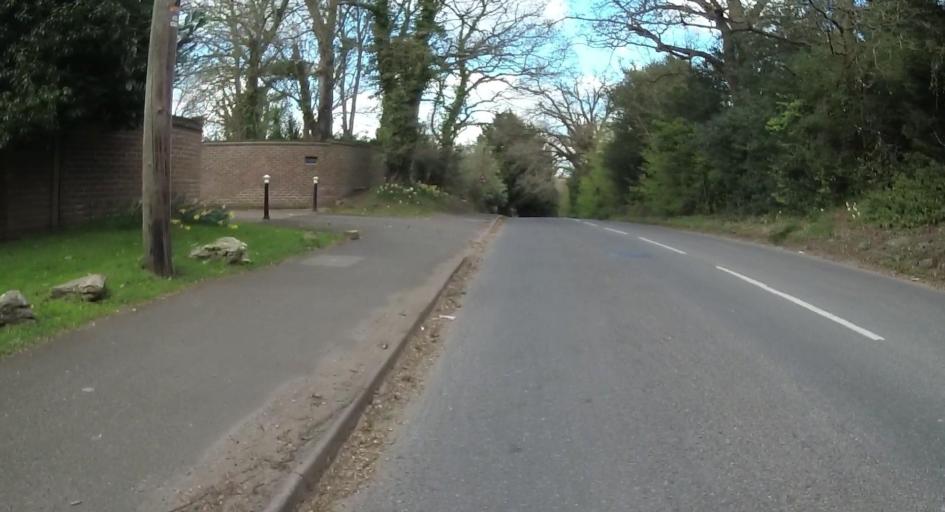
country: GB
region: England
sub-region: Surrey
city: West Byfleet
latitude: 51.3511
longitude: -0.5143
